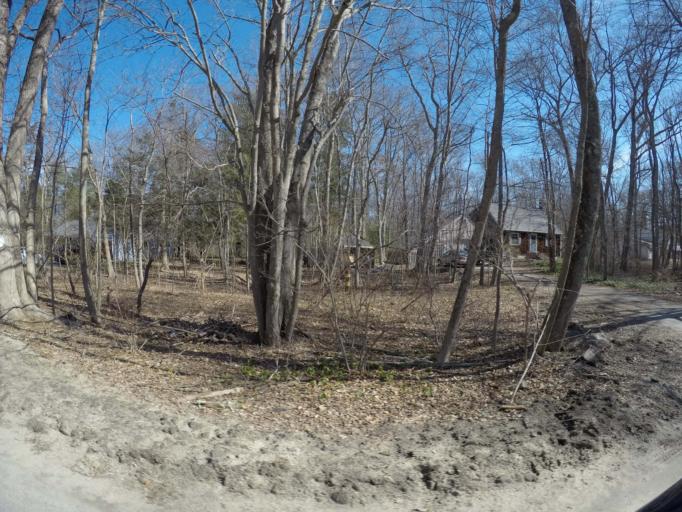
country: US
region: Massachusetts
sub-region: Norfolk County
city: Sharon
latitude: 42.0930
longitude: -71.1565
